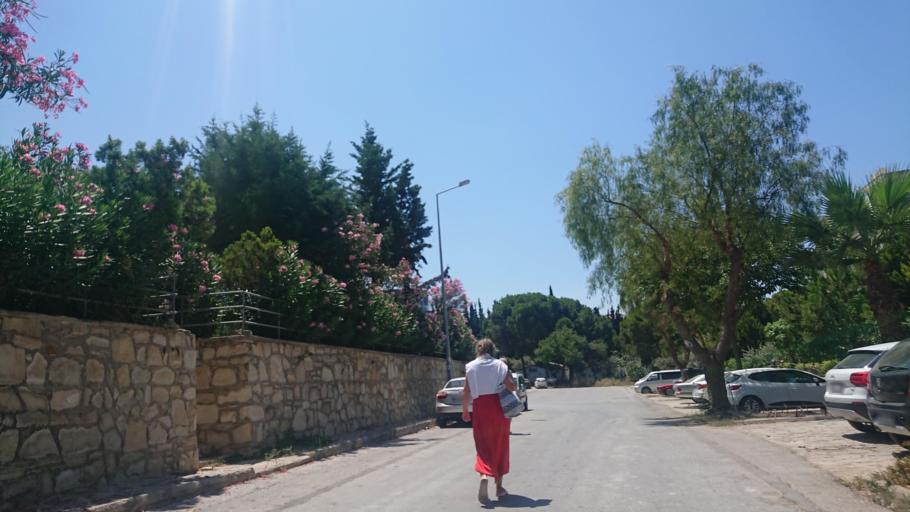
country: TR
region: Aydin
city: Kusadasi
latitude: 37.8695
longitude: 27.2665
